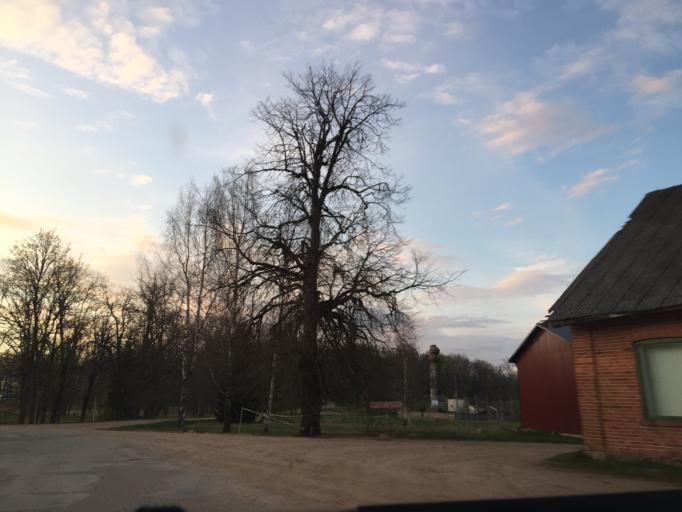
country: LV
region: Aluksnes Rajons
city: Aluksne
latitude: 57.2700
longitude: 26.9290
